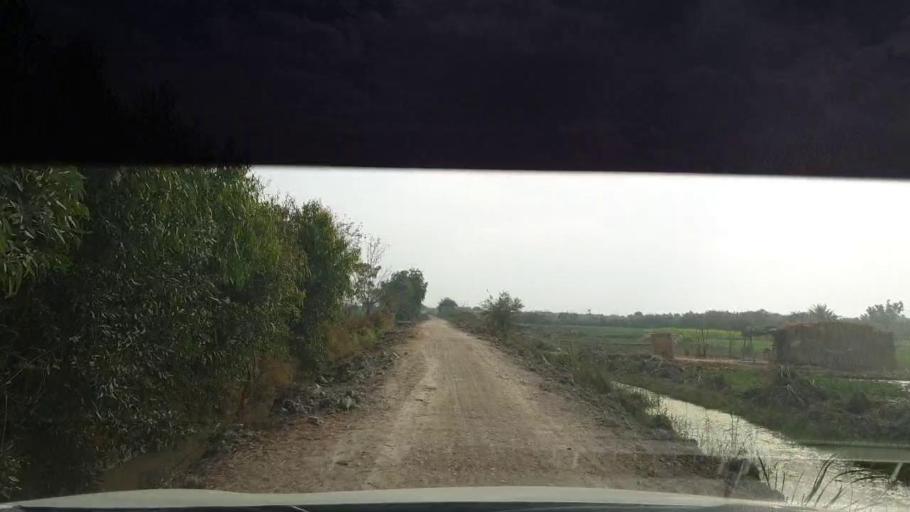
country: PK
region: Sindh
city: Berani
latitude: 25.7519
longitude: 68.8769
